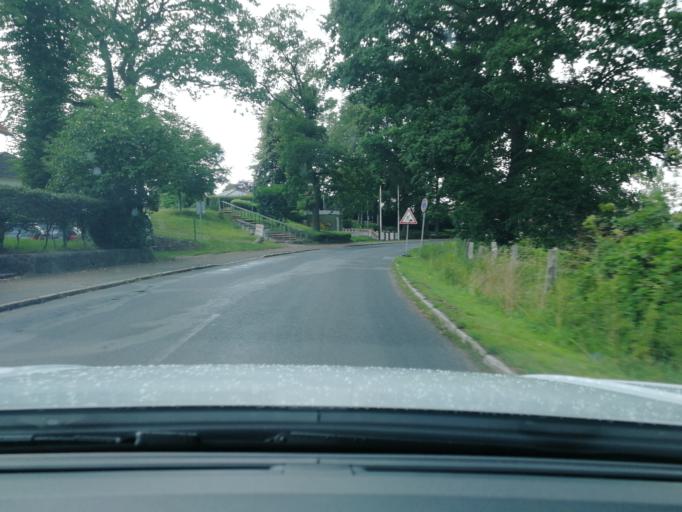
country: DE
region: Schleswig-Holstein
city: Grossensee
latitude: 53.6112
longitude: 10.3430
